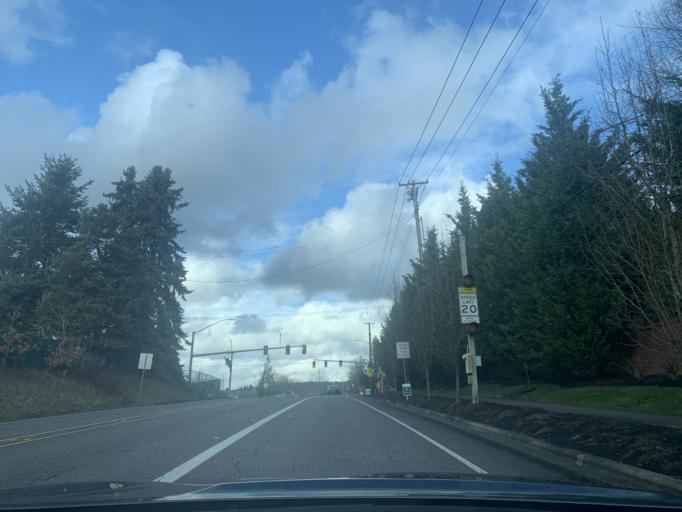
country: US
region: Oregon
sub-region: Washington County
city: Cedar Mill
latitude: 45.5475
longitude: -122.8106
